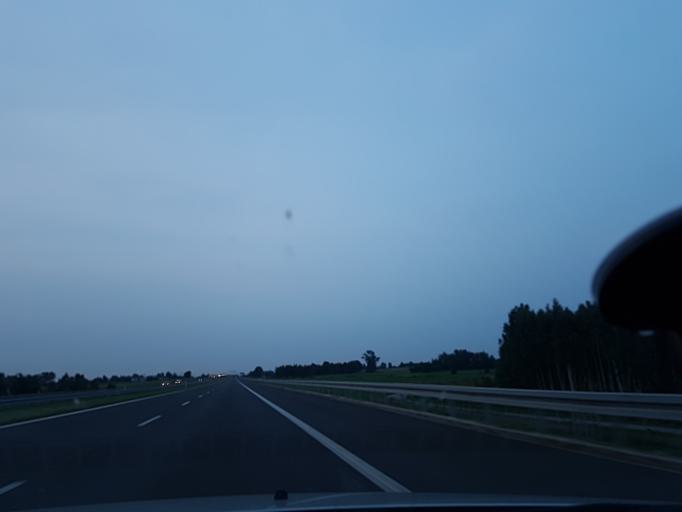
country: PL
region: Lodz Voivodeship
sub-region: Powiat zgierski
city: Strykow
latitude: 51.9351
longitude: 19.6132
